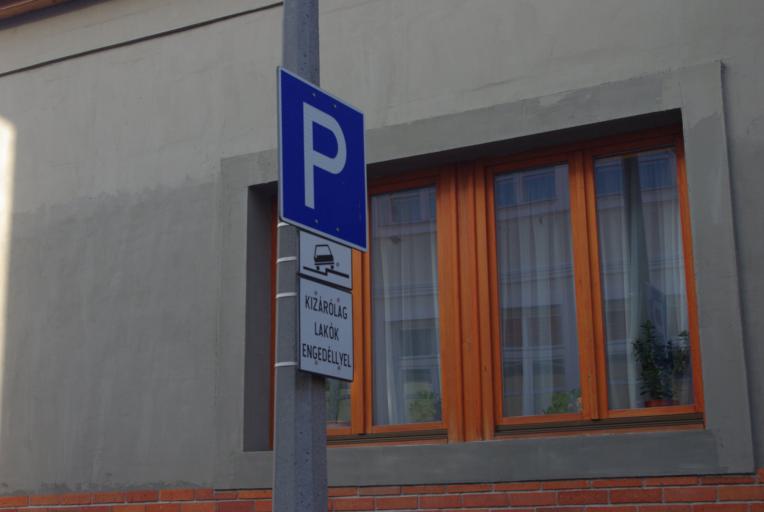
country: HU
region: Borsod-Abauj-Zemplen
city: Satoraljaujhely
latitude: 48.3948
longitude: 21.6548
